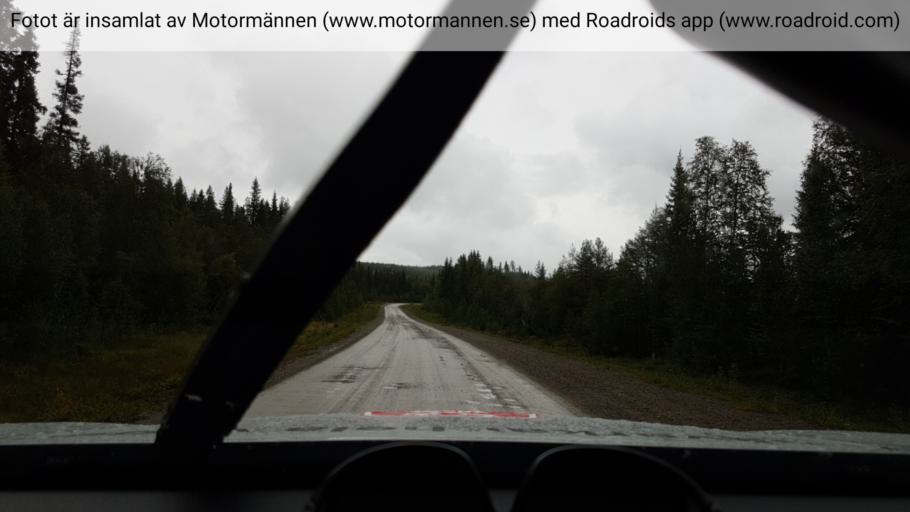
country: SE
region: Vaesterbotten
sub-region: Asele Kommun
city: Insjon
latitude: 64.8195
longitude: 17.4877
